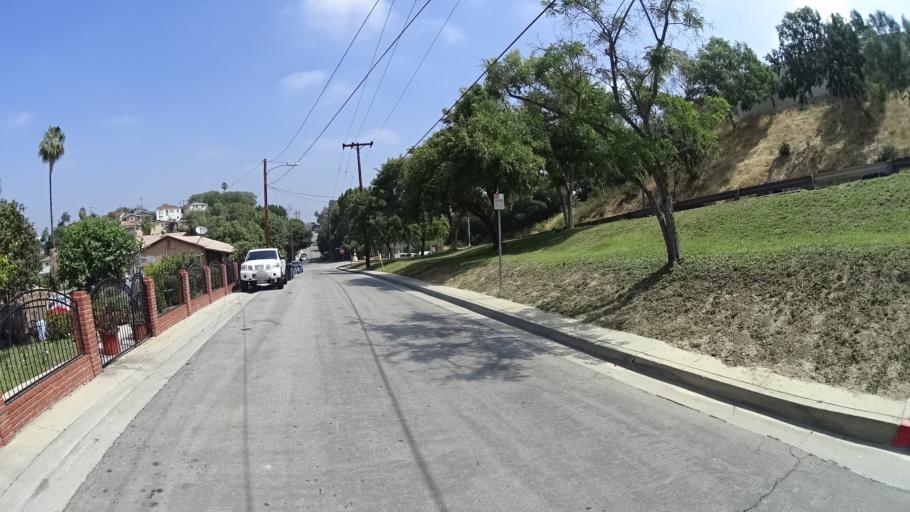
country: US
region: California
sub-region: Los Angeles County
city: Belvedere
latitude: 34.0573
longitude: -118.1694
